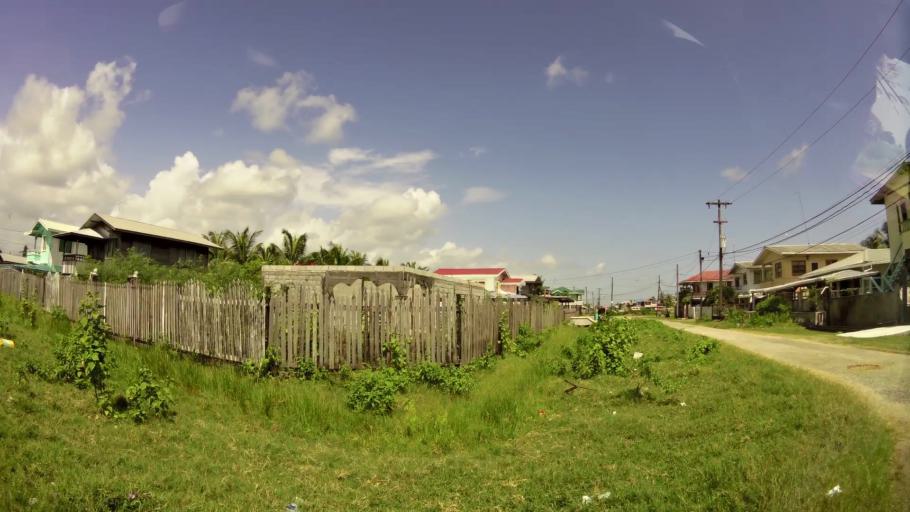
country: GY
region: Demerara-Mahaica
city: Mahaica Village
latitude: 6.7707
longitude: -58.0091
